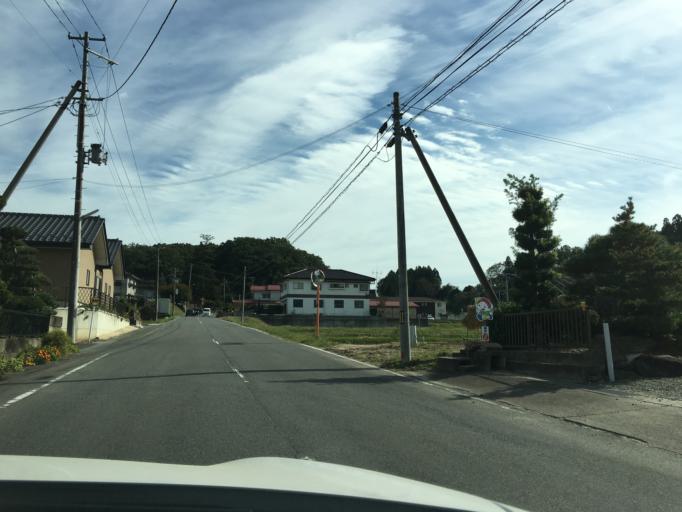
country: JP
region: Fukushima
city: Nihommatsu
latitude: 37.5900
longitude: 140.4622
